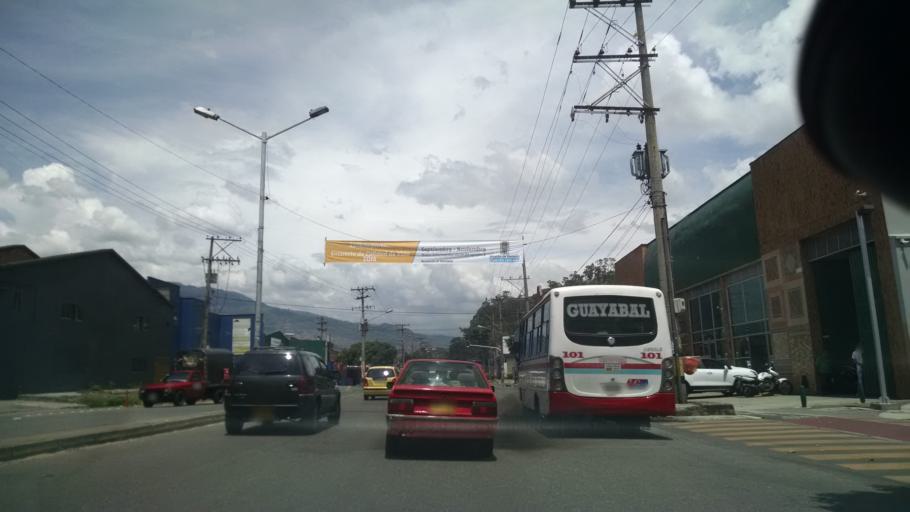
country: CO
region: Antioquia
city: Medellin
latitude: 6.2323
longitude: -75.5827
